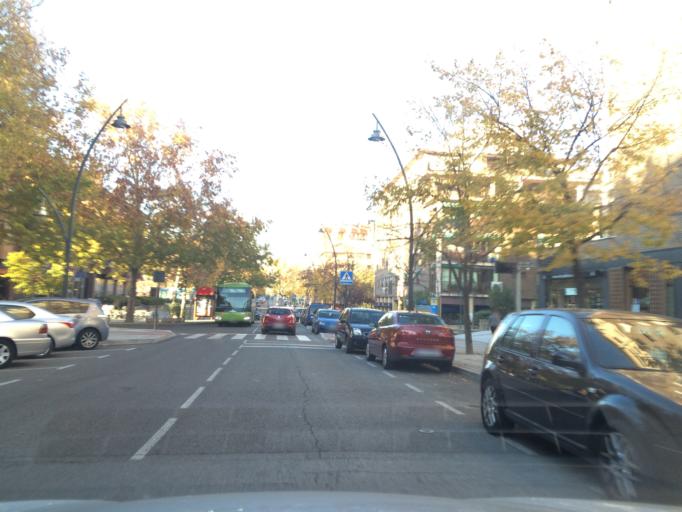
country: ES
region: Madrid
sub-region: Provincia de Madrid
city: Tres Cantos
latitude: 40.5948
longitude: -3.7035
